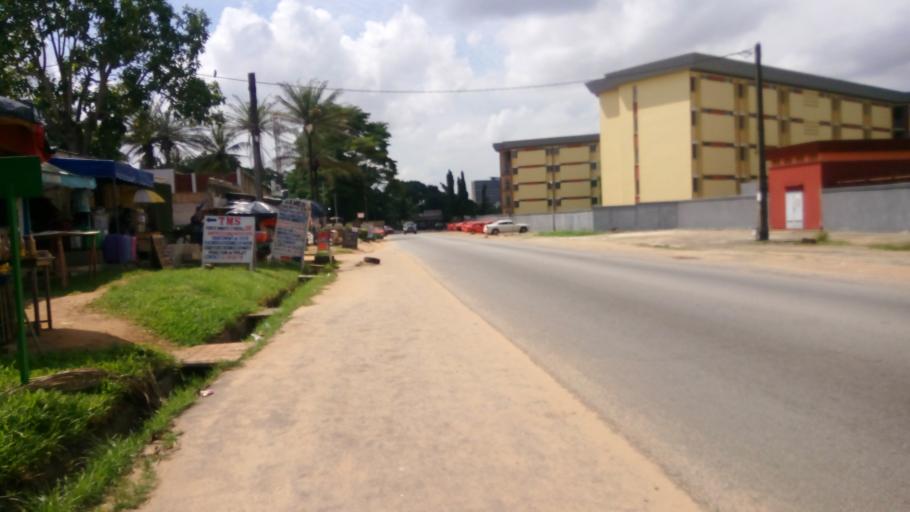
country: CI
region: Lagunes
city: Abidjan
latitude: 5.3377
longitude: -3.9962
